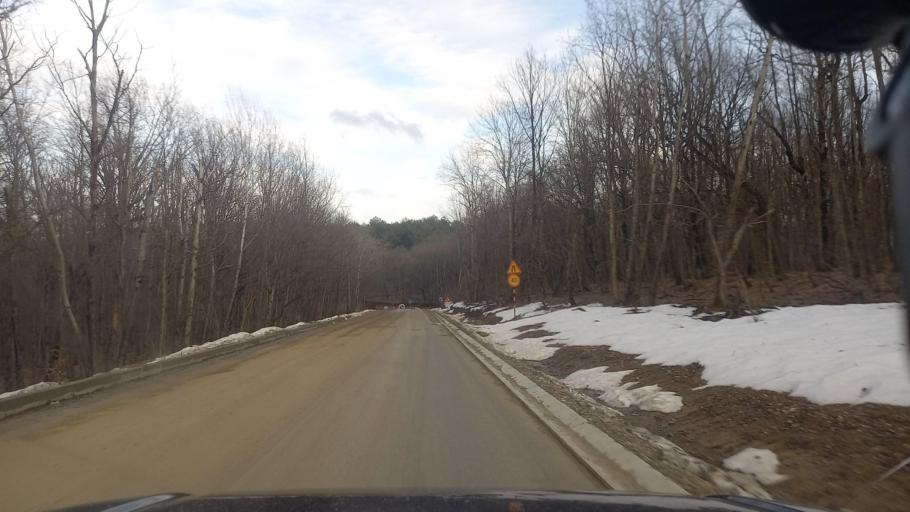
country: RU
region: Krasnodarskiy
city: Goryachiy Klyuch
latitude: 44.6976
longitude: 38.9881
